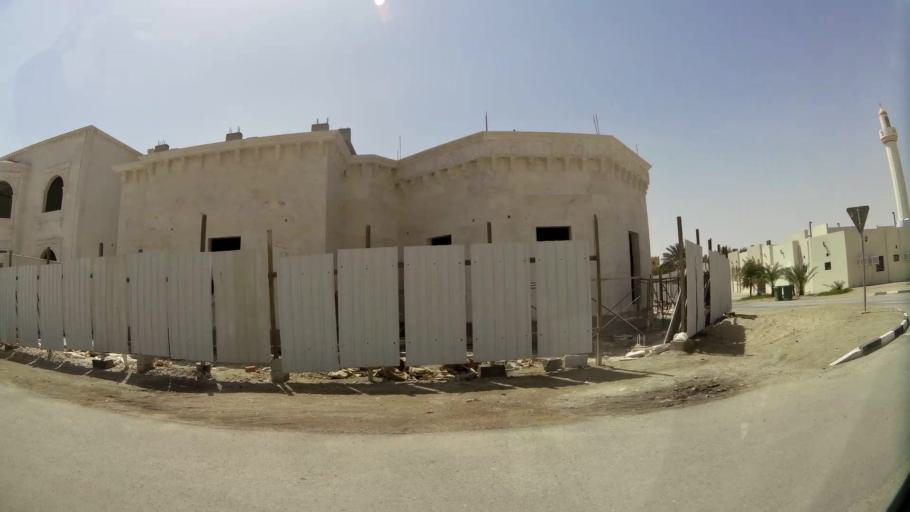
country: QA
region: Baladiyat Umm Salal
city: Umm Salal Muhammad
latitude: 25.3705
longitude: 51.4315
